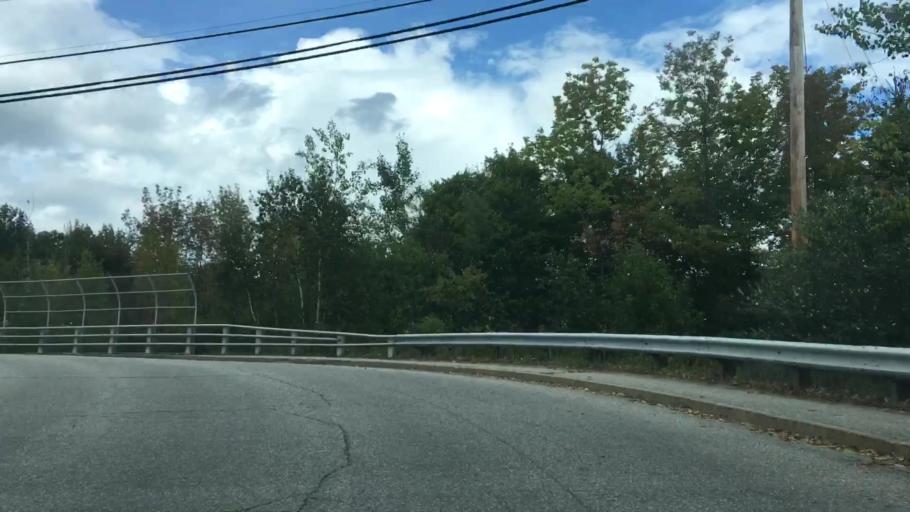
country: US
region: New Hampshire
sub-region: Coos County
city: Berlin
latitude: 44.4493
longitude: -71.1899
